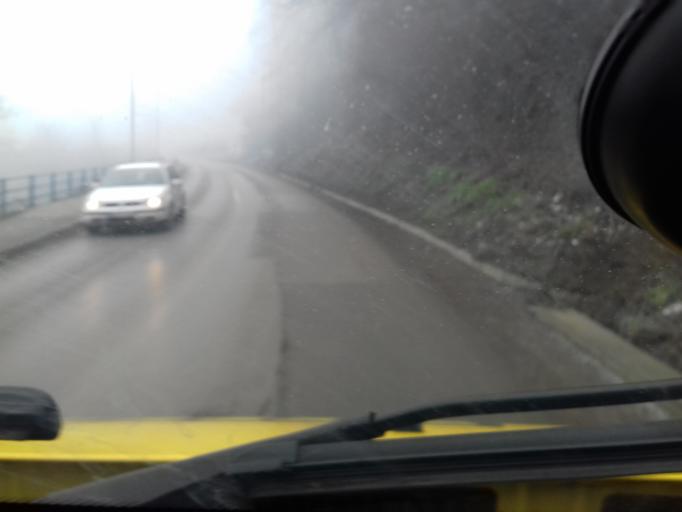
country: BA
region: Federation of Bosnia and Herzegovina
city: Visoko
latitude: 43.9972
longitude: 18.1659
